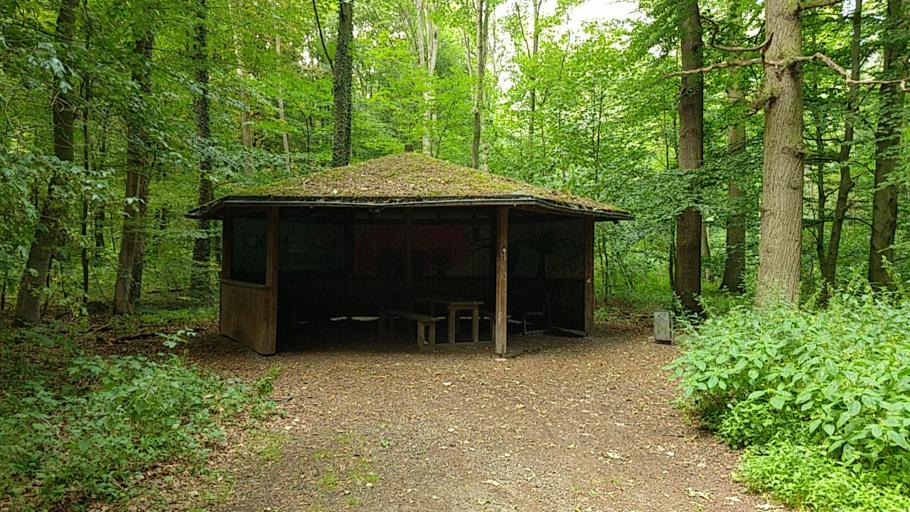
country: DE
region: Lower Saxony
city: Wunstorf
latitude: 52.4378
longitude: 9.3964
